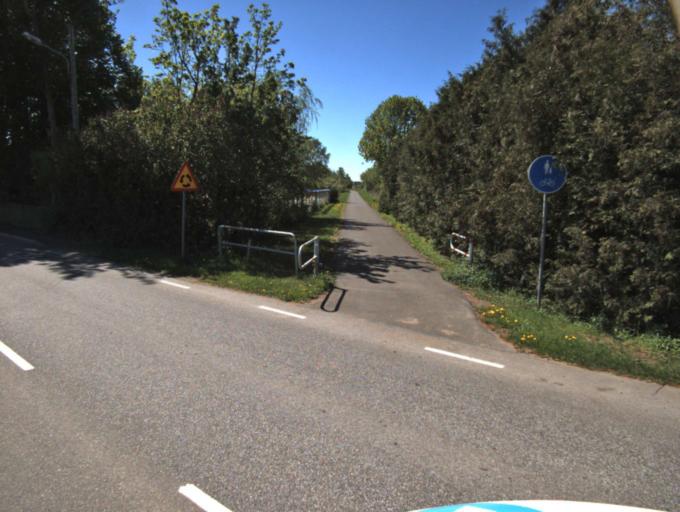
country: SE
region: Skane
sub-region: Kristianstads Kommun
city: Norra Asum
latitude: 55.9512
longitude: 14.1541
